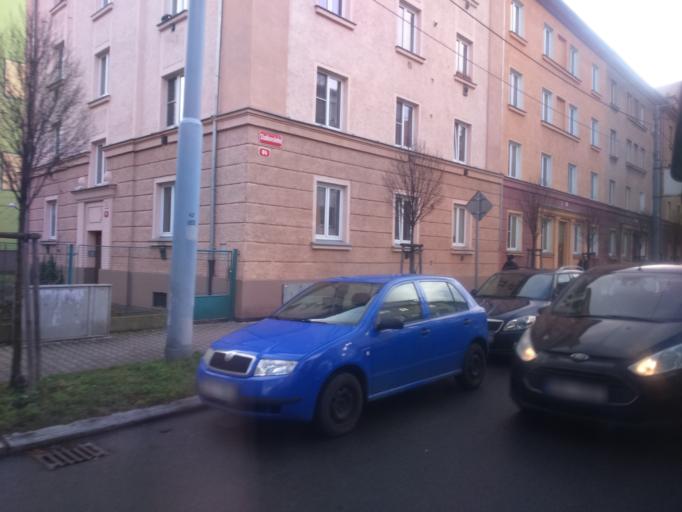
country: CZ
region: Plzensky
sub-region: Okres Plzen-Mesto
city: Pilsen
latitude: 49.7410
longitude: 13.3942
